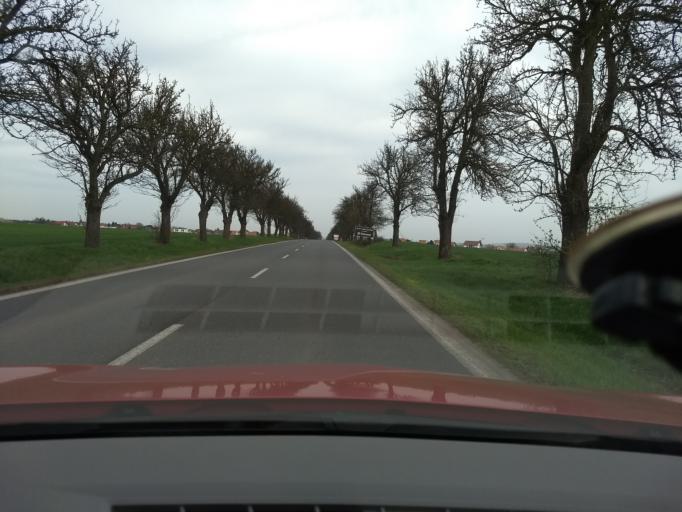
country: CZ
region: Central Bohemia
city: Horomerice
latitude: 50.1260
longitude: 14.3481
